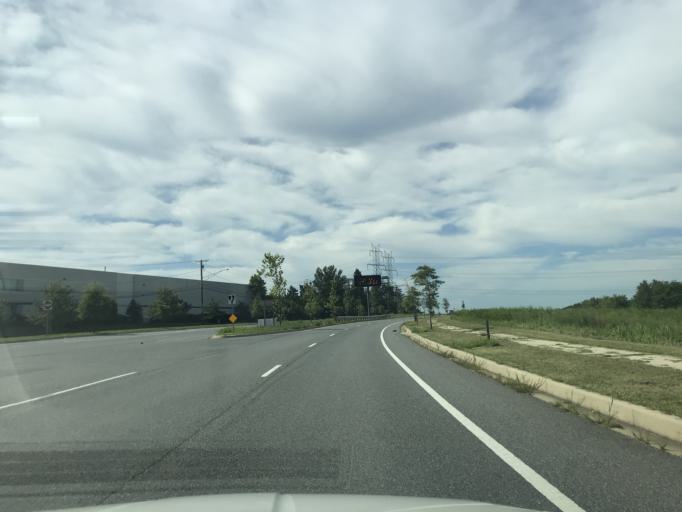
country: US
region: Maryland
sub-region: Prince George's County
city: West Laurel
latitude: 39.0753
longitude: -76.8858
